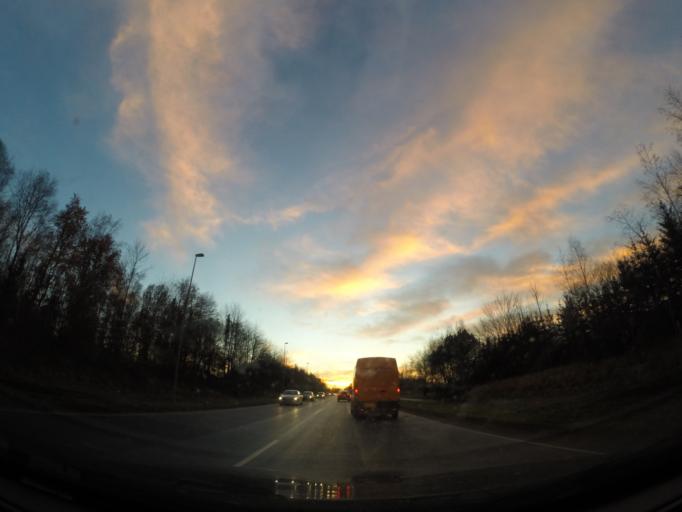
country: DK
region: Capital Region
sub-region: Ballerup Kommune
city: Ballerup
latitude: 55.7460
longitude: 12.3926
